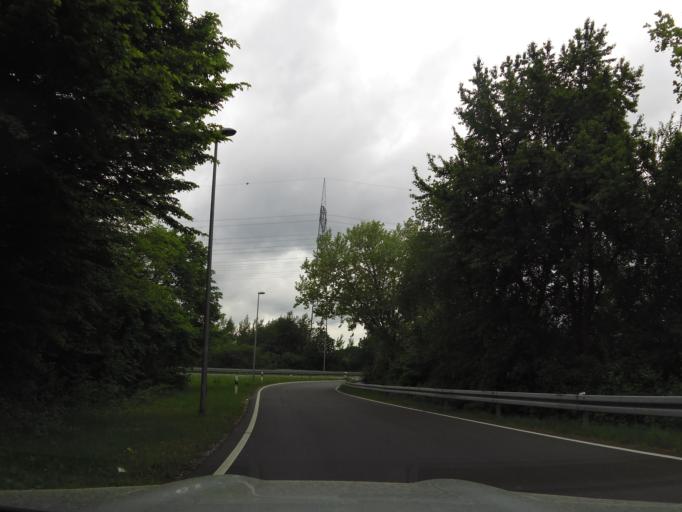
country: DE
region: Hesse
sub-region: Regierungsbezirk Darmstadt
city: Florsheim
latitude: 50.0052
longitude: 8.4272
